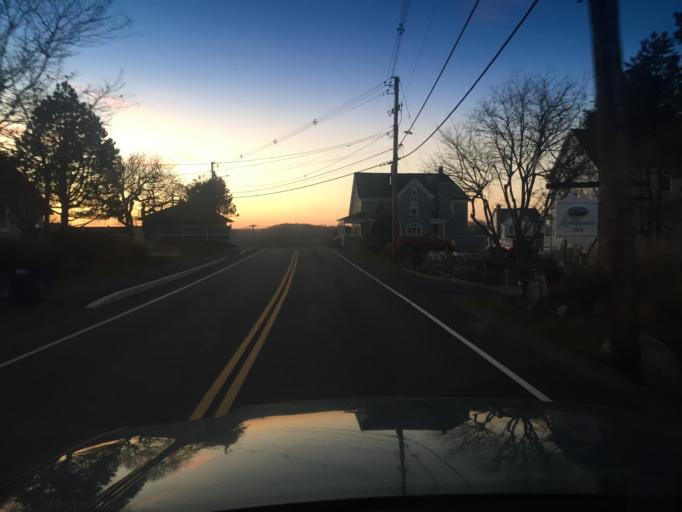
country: US
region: Maine
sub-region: York County
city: York Beach
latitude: 43.1691
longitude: -70.6099
